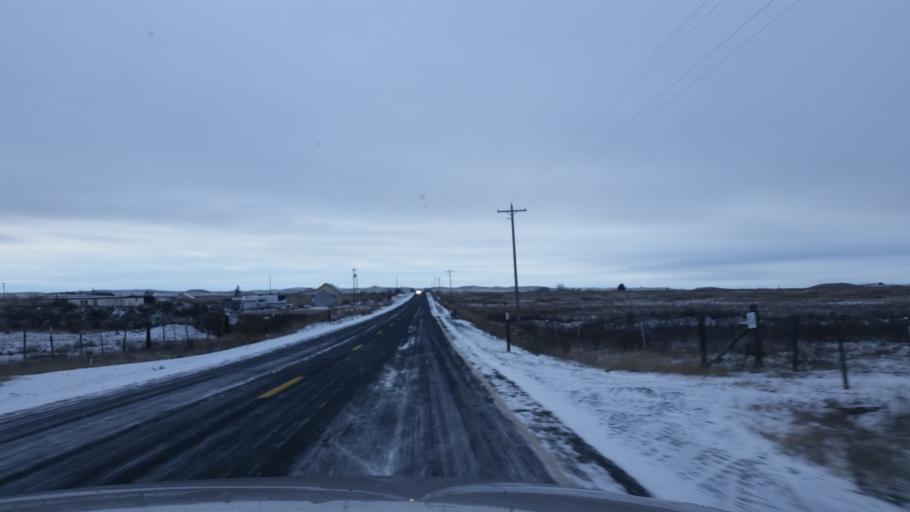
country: US
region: Washington
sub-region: Spokane County
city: Cheney
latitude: 47.4057
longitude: -117.4885
